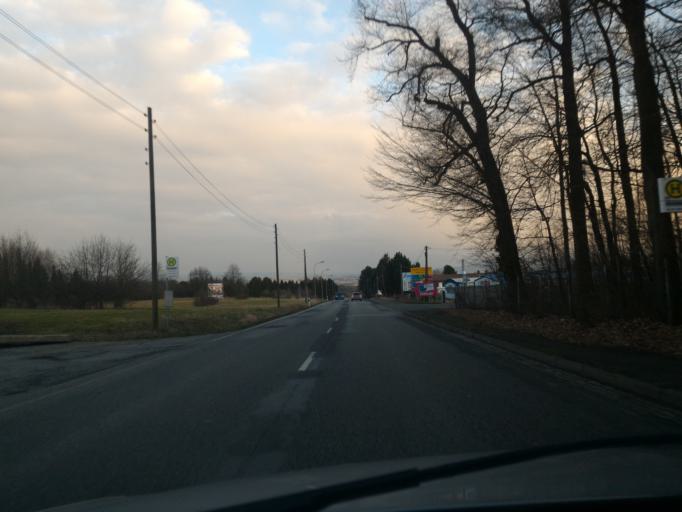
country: DE
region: Saxony
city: Mittelherwigsdorf
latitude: 50.9073
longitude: 14.7667
